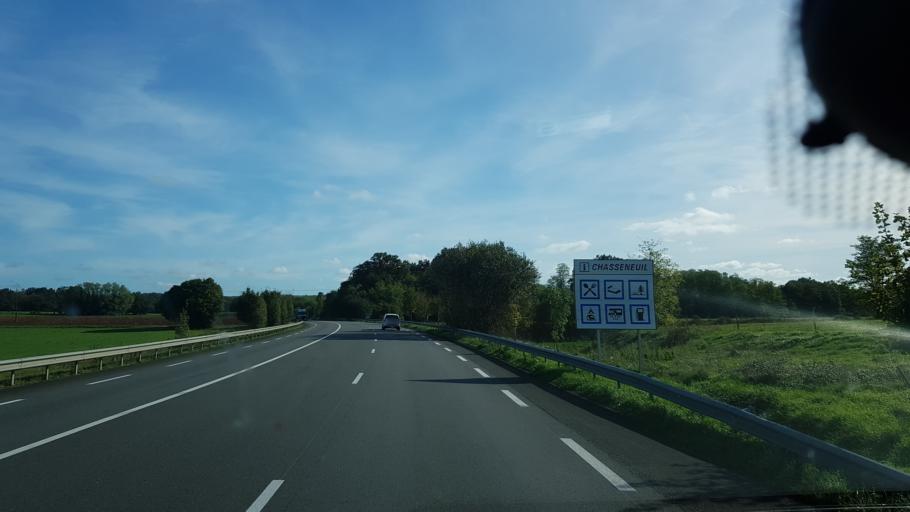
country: FR
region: Poitou-Charentes
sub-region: Departement de la Charente
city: Chasseneuil-sur-Bonnieure
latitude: 45.8398
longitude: 0.4614
